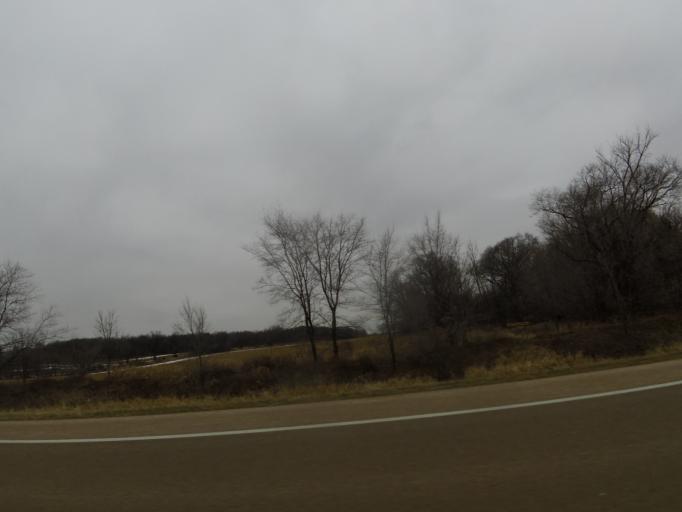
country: US
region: Minnesota
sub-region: Carver County
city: Watertown
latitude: 44.9668
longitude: -93.7903
